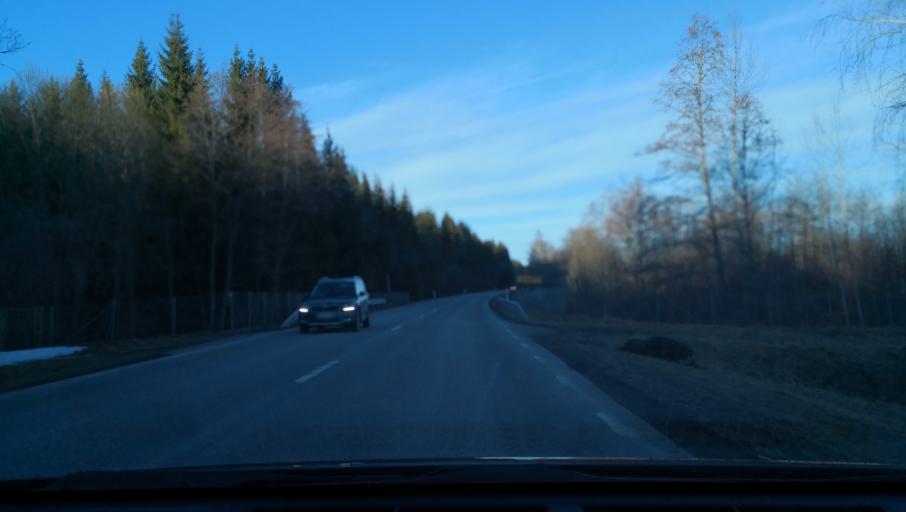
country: SE
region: Uppsala
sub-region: Osthammars Kommun
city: Gimo
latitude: 60.1915
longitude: 18.1901
